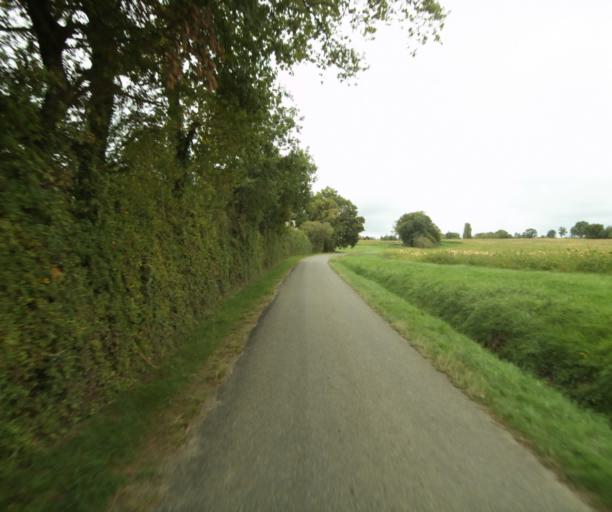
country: FR
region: Midi-Pyrenees
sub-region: Departement du Gers
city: Eauze
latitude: 43.8965
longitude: 0.0833
